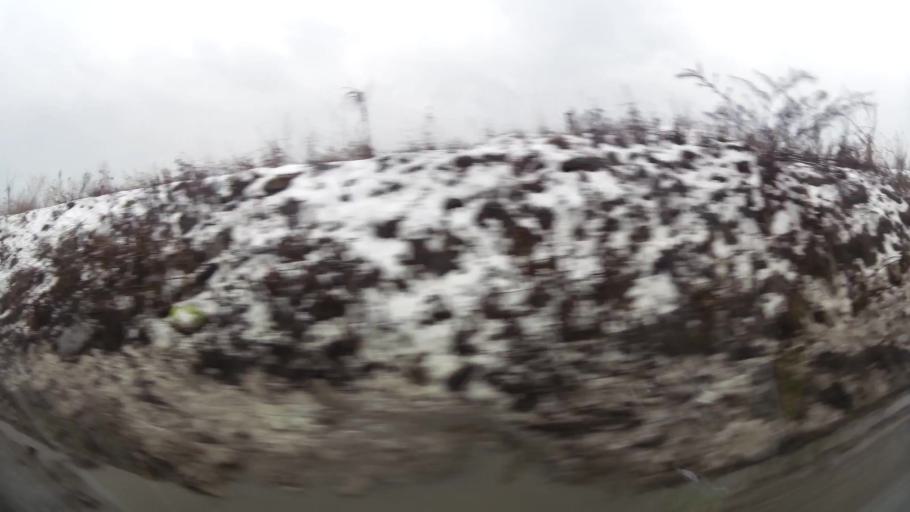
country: BG
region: Sofia-Capital
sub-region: Stolichna Obshtina
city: Sofia
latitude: 42.6954
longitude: 23.2551
